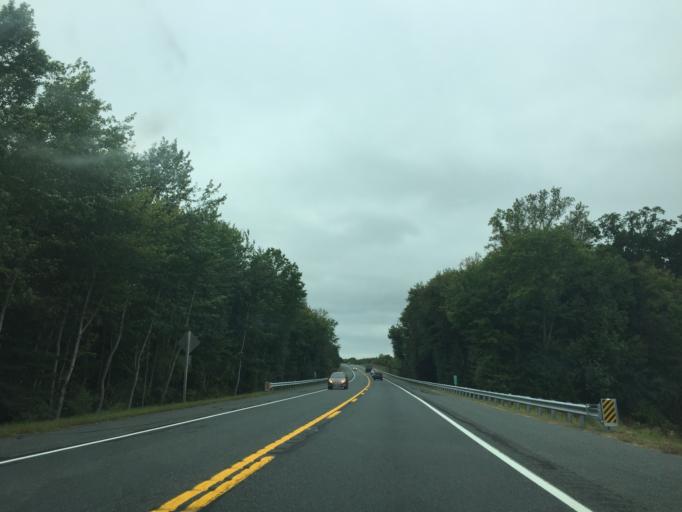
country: US
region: Maryland
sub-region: Harford County
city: Bel Air North
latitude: 39.5749
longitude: -76.3746
